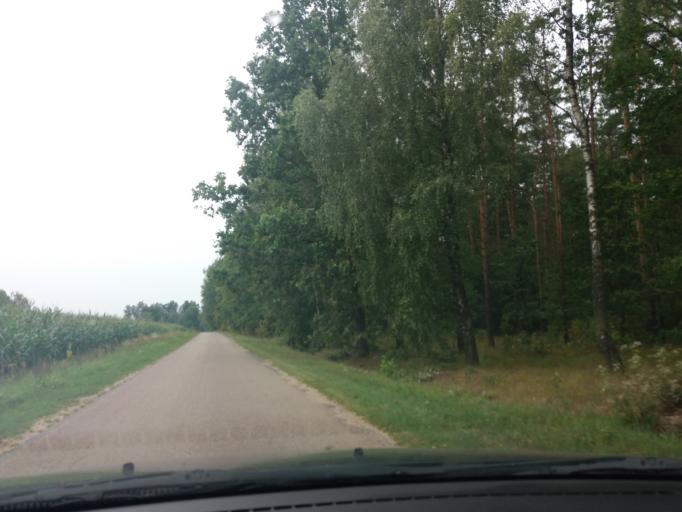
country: PL
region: Masovian Voivodeship
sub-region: Powiat mlawski
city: Wieczfnia Koscielna
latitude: 53.2338
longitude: 20.4902
